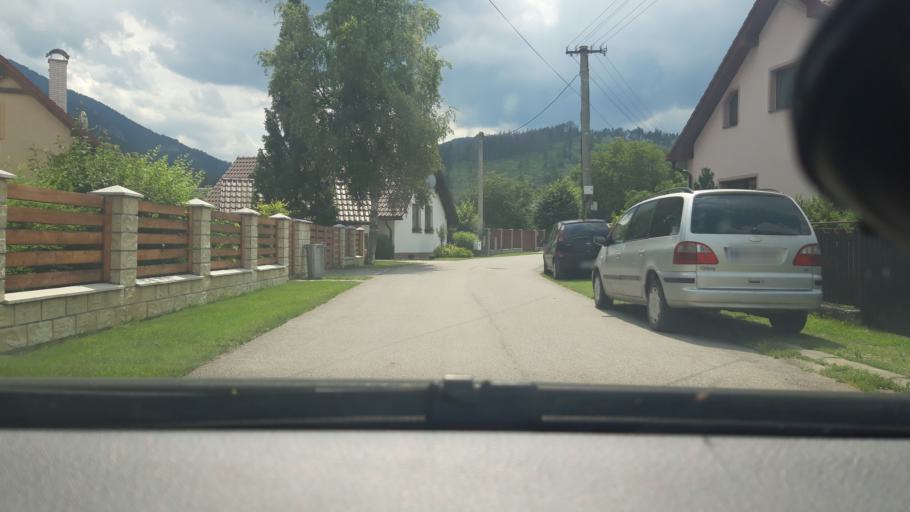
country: SK
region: Zilinsky
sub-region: Okres Martin
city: Martin
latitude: 48.9353
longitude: 18.9251
